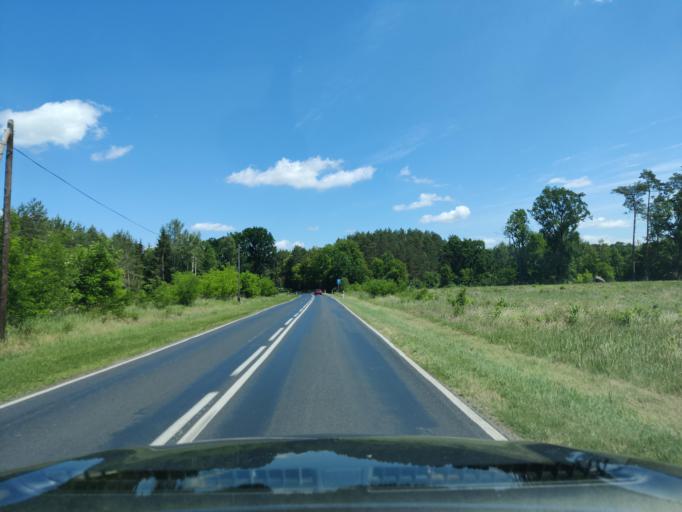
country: PL
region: Greater Poland Voivodeship
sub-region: Powiat nowotomyski
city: Nowy Tomysl
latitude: 52.2324
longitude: 16.1150
